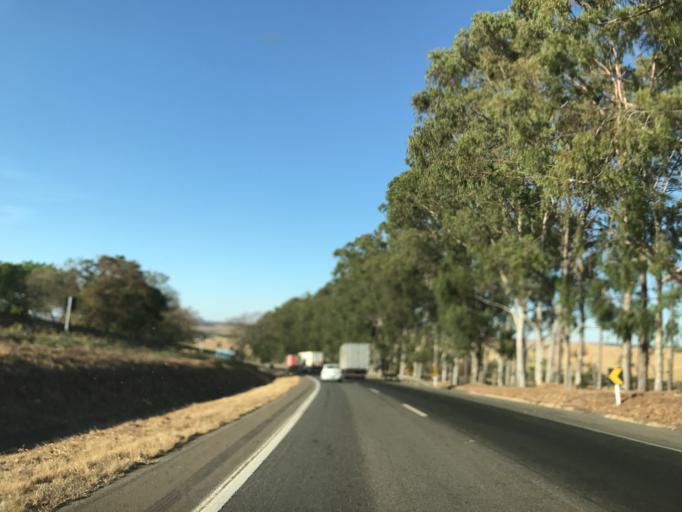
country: BR
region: Goias
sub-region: Hidrolandia
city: Hidrolandia
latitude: -16.9385
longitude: -49.2535
